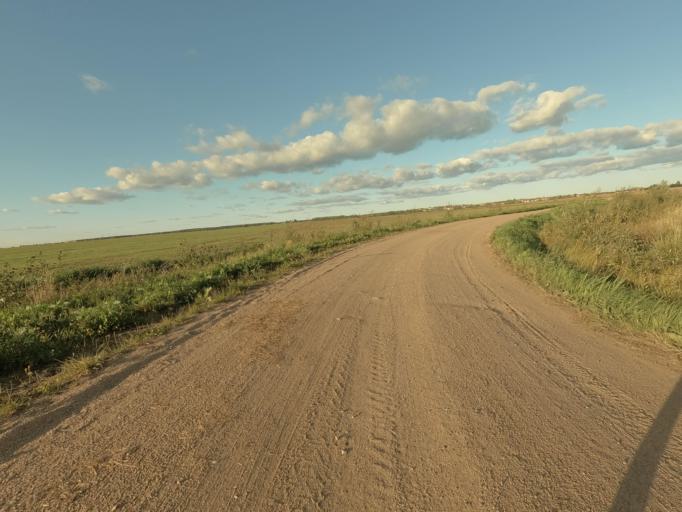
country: RU
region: Leningrad
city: Otradnoye
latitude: 59.8621
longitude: 30.7521
